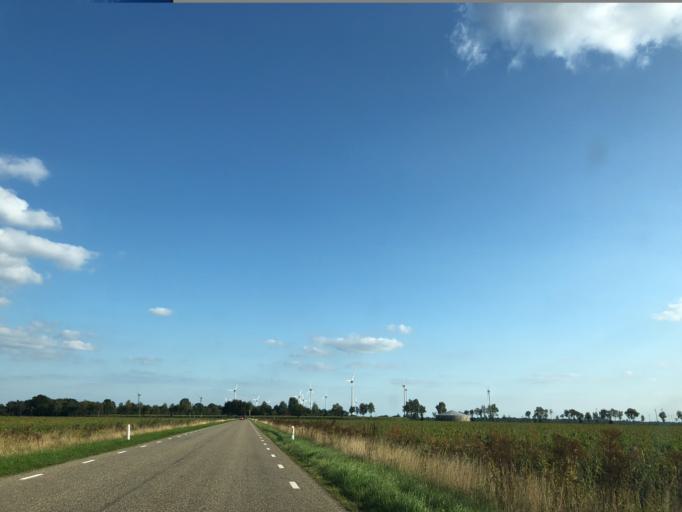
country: NL
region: Groningen
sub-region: Gemeente Vlagtwedde
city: Sellingen
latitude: 53.0007
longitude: 7.1879
